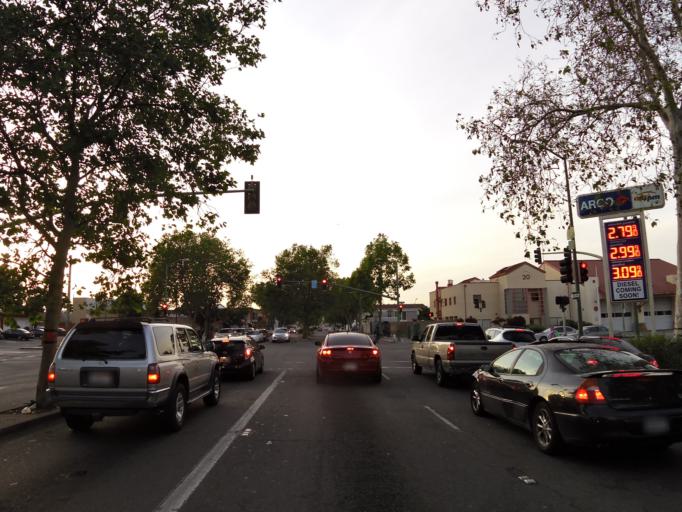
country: US
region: California
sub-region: Alameda County
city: San Leandro
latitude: 37.7441
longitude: -122.1703
